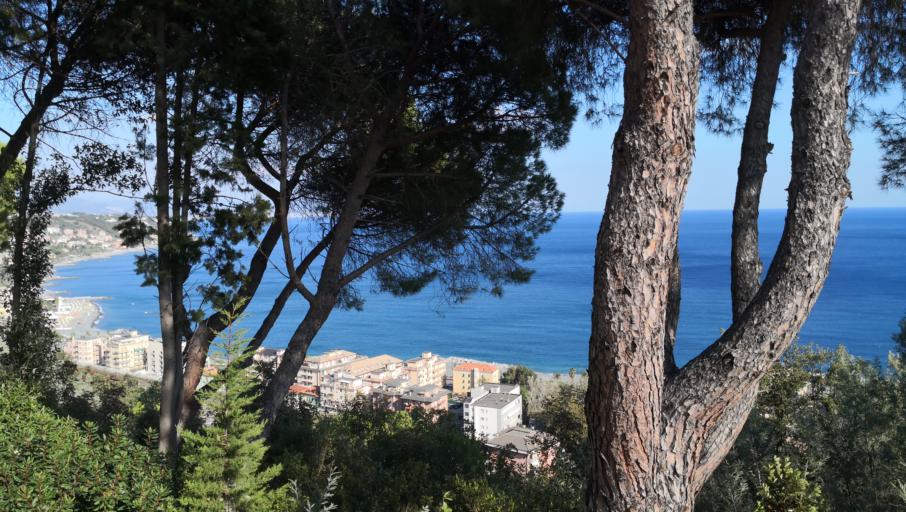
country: IT
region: Liguria
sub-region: Provincia di Genova
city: Cogoleto
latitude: 44.3840
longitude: 8.6321
